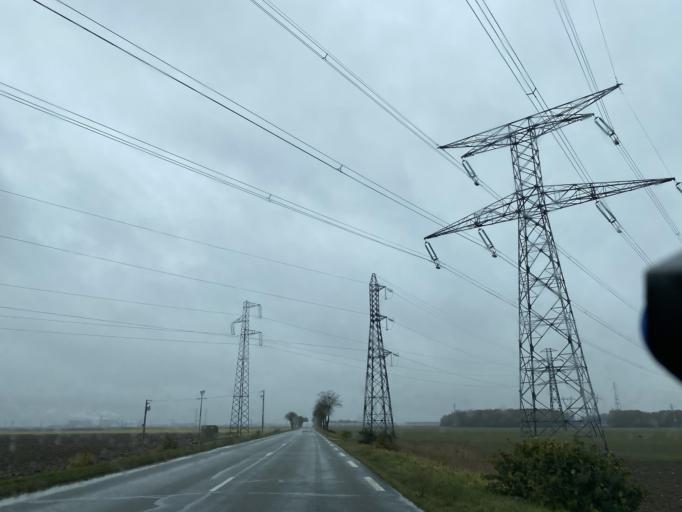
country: FR
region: Centre
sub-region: Departement du Loiret
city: Artenay
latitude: 48.1148
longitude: 1.8602
